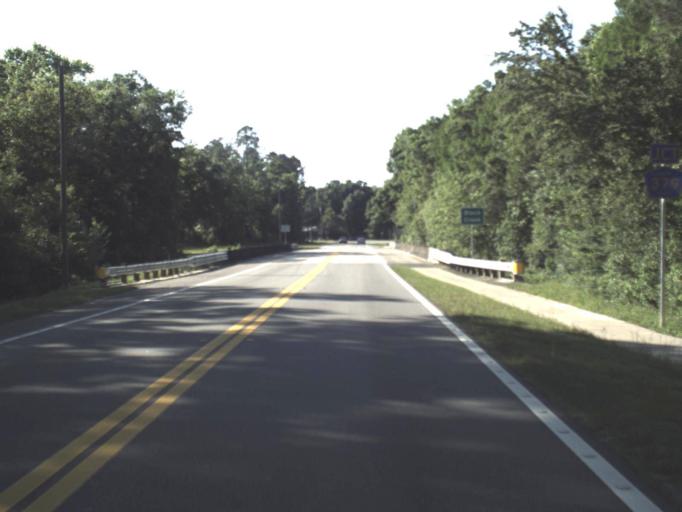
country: US
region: Florida
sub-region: Gulf County
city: Wewahitchka
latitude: 30.0255
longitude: -84.9813
